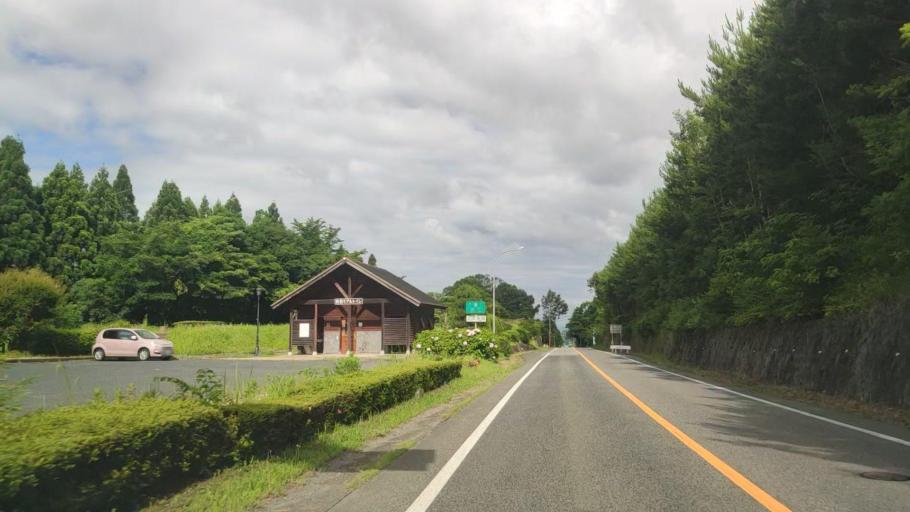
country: JP
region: Tottori
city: Yonago
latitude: 35.4229
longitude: 133.4222
